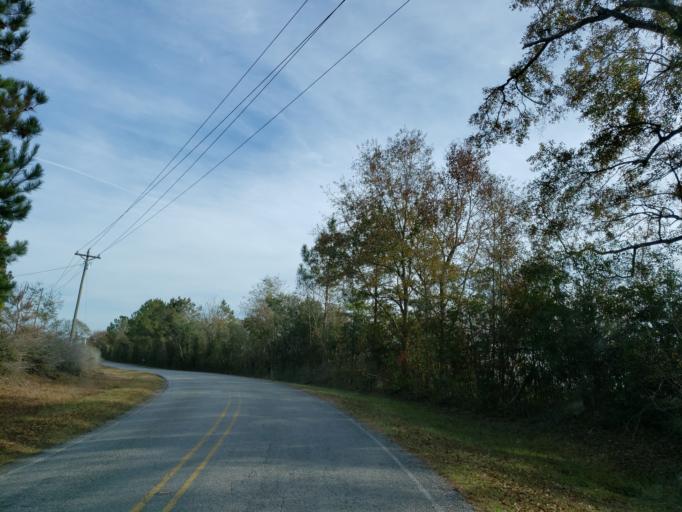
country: US
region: Mississippi
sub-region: Forrest County
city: Rawls Springs
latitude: 31.4087
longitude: -89.4069
